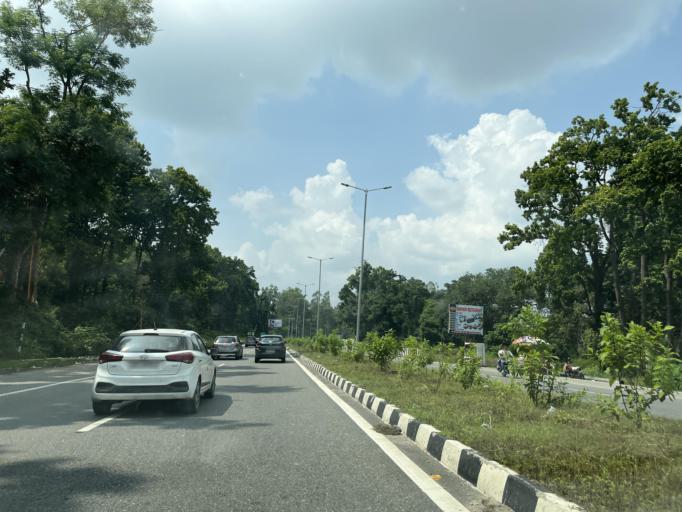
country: IN
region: Uttarakhand
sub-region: Dehradun
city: Raipur
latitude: 30.2489
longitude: 78.0949
